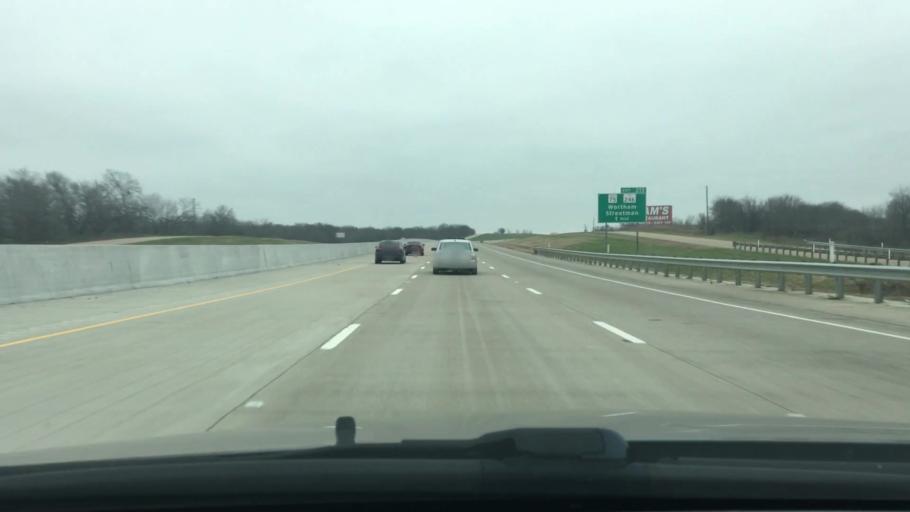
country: US
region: Texas
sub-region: Freestone County
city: Wortham
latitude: 31.8914
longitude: -96.3589
